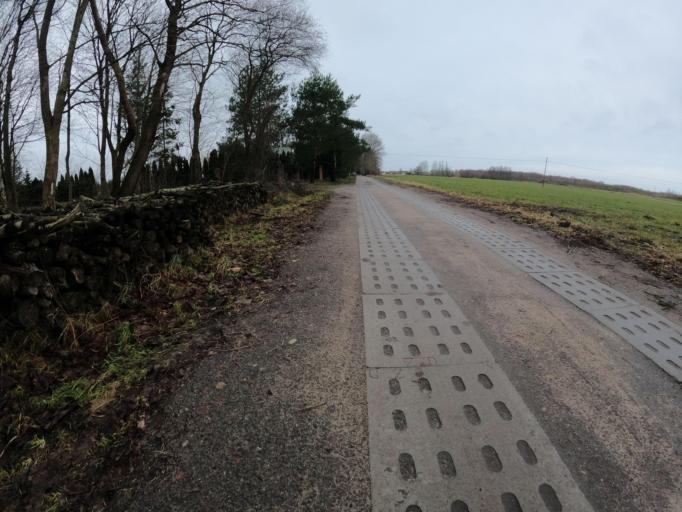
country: PL
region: West Pomeranian Voivodeship
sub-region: Powiat slawienski
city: Darlowo
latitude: 54.4129
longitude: 16.4405
